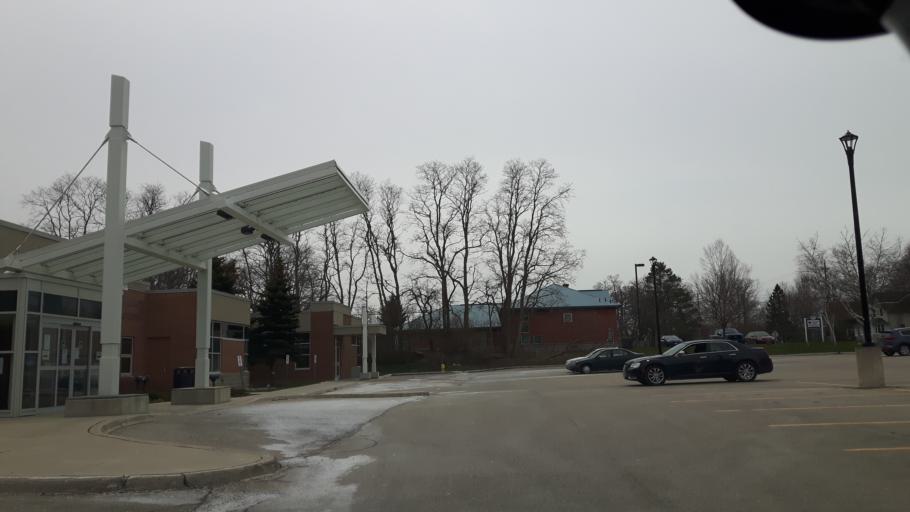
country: CA
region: Ontario
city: Goderich
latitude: 43.7498
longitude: -81.7041
